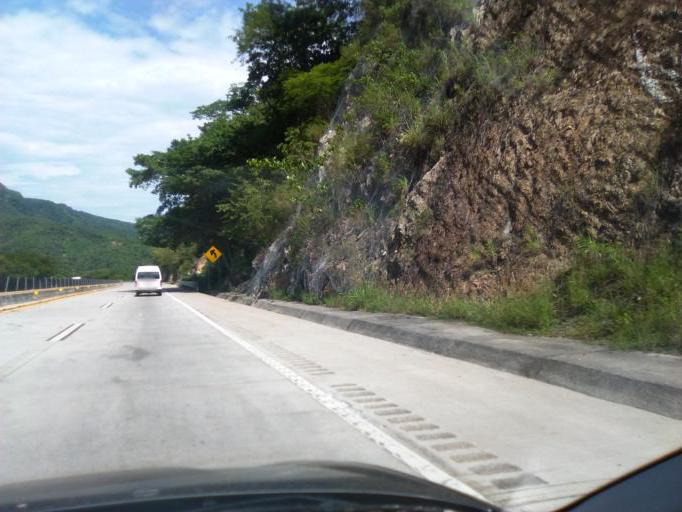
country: MX
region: Guerrero
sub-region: Acapulco de Juarez
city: Pueblo Madero (El Playon)
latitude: 17.0903
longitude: -99.5970
